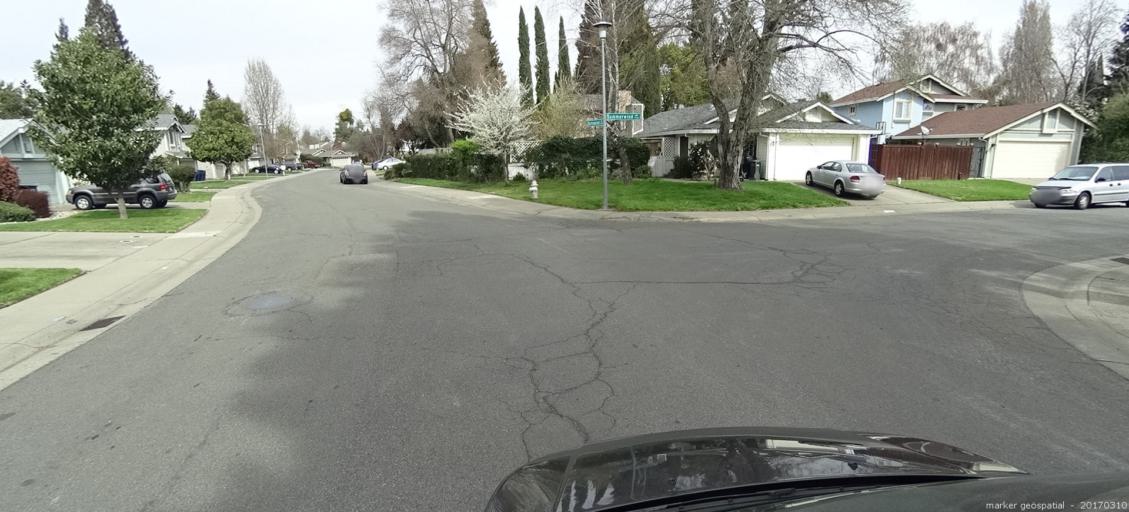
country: US
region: California
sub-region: Sacramento County
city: Parkway
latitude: 38.4847
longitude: -121.5315
